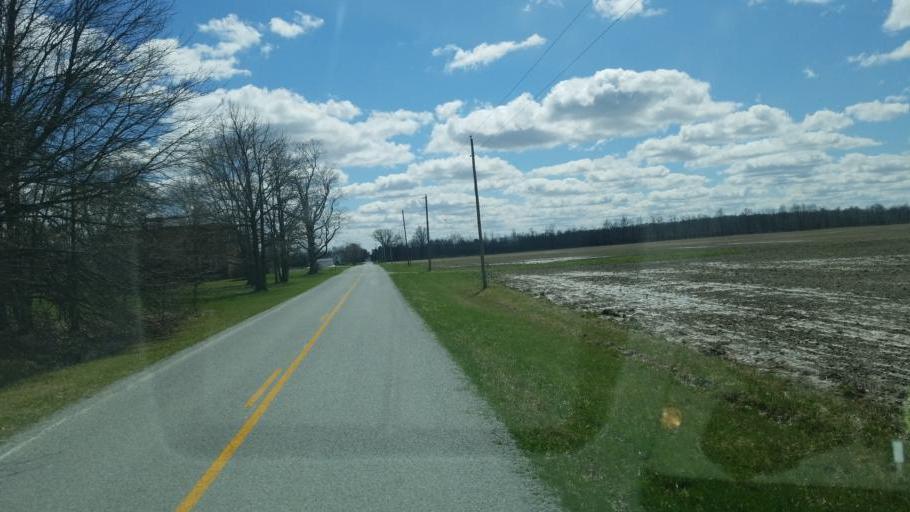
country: US
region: Ohio
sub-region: Hardin County
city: Forest
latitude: 40.8012
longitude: -83.5765
